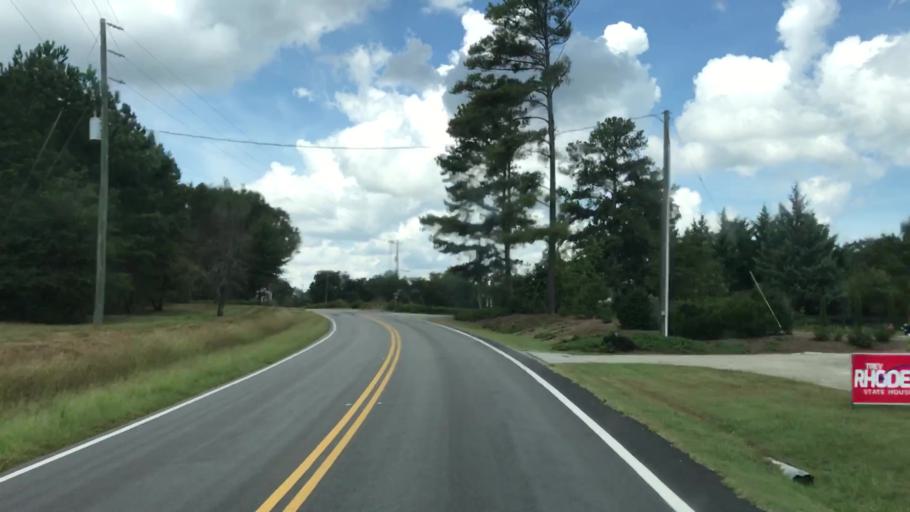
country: US
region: Georgia
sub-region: Greene County
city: Union Point
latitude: 33.5533
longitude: -83.1038
